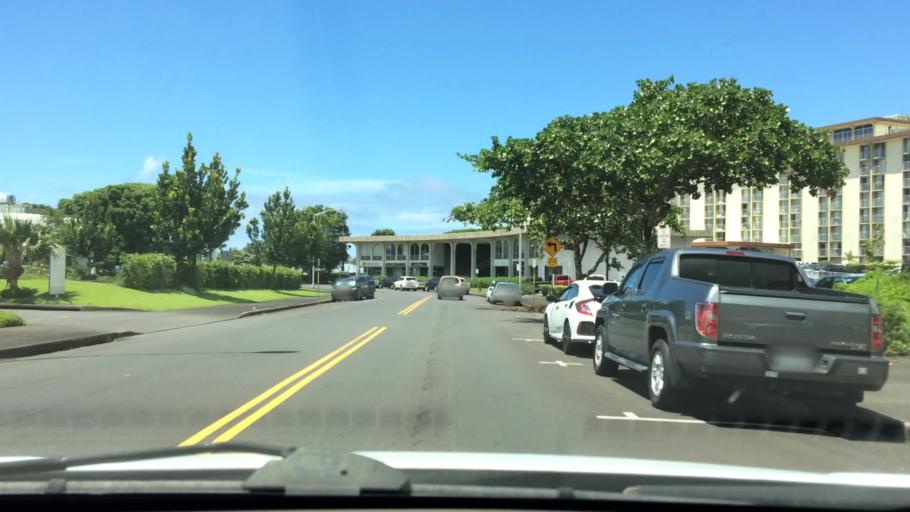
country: US
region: Hawaii
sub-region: Hawaii County
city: Hilo
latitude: 19.7169
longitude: -155.0780
